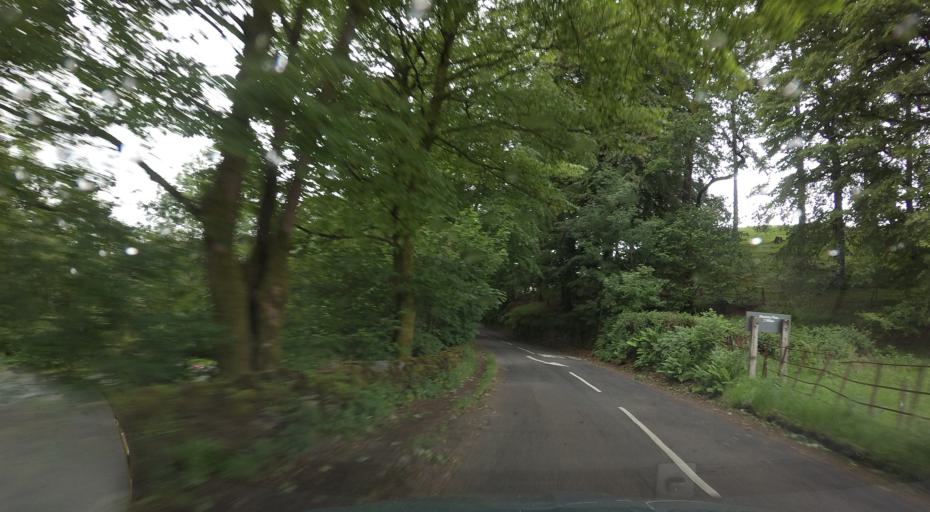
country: GB
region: England
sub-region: Cumbria
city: Keswick
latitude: 54.5225
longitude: -3.1464
